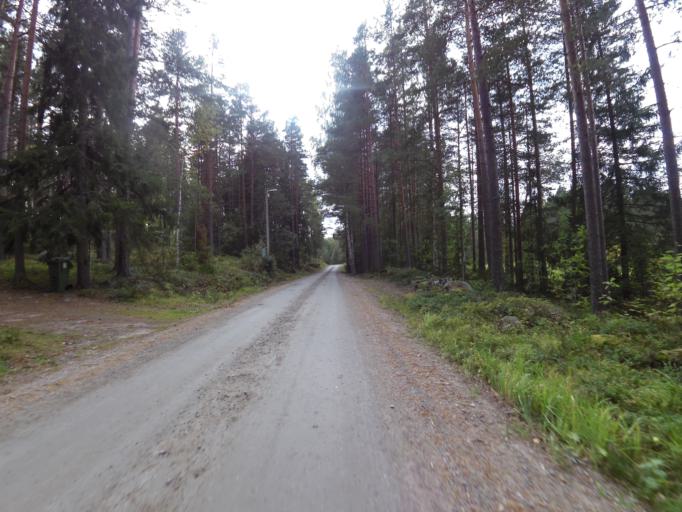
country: SE
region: Gaevleborg
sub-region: Sandvikens Kommun
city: Sandviken
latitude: 60.7310
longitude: 16.8216
